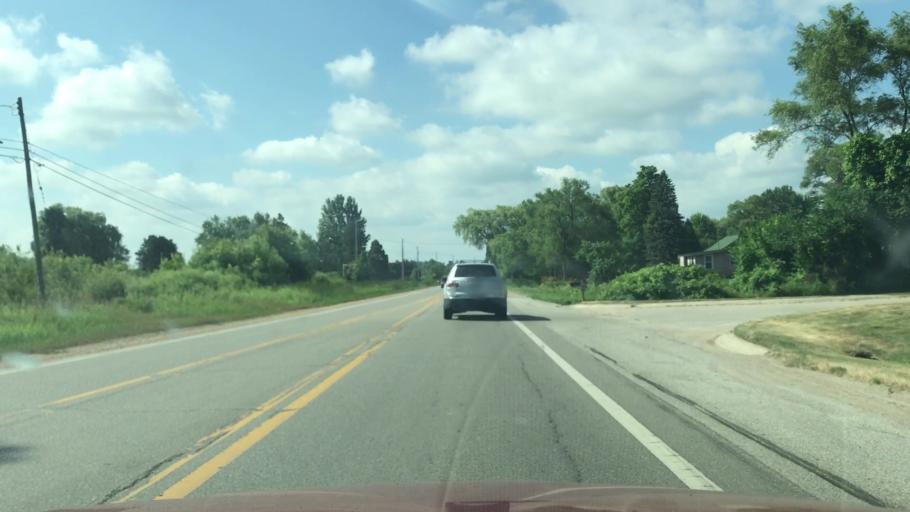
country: US
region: Michigan
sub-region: Kent County
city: Kent City
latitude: 43.3067
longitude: -85.8106
